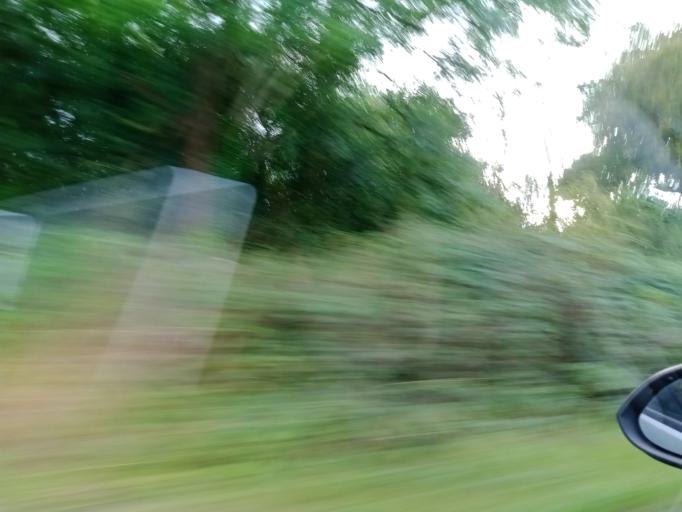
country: IE
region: Leinster
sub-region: Laois
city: Mountmellick
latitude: 53.1313
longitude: -7.3943
